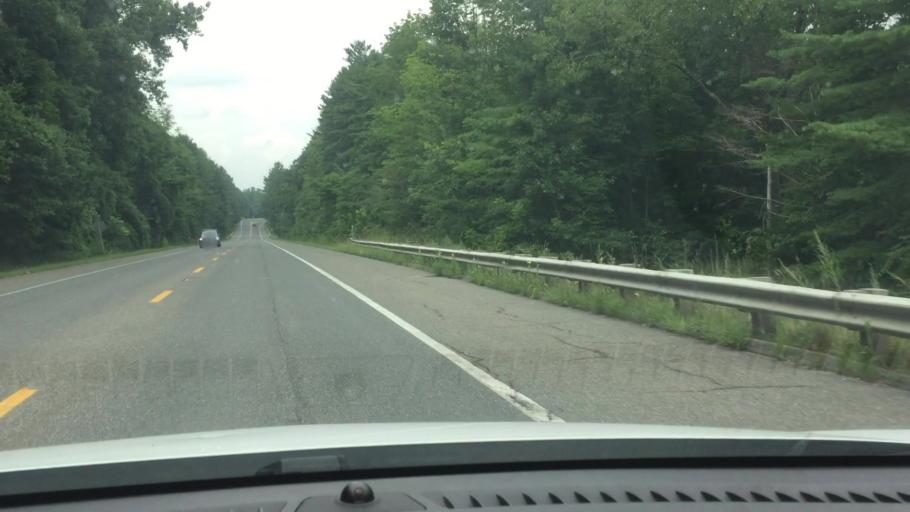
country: US
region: Massachusetts
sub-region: Berkshire County
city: Lenox
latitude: 42.3300
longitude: -73.2874
